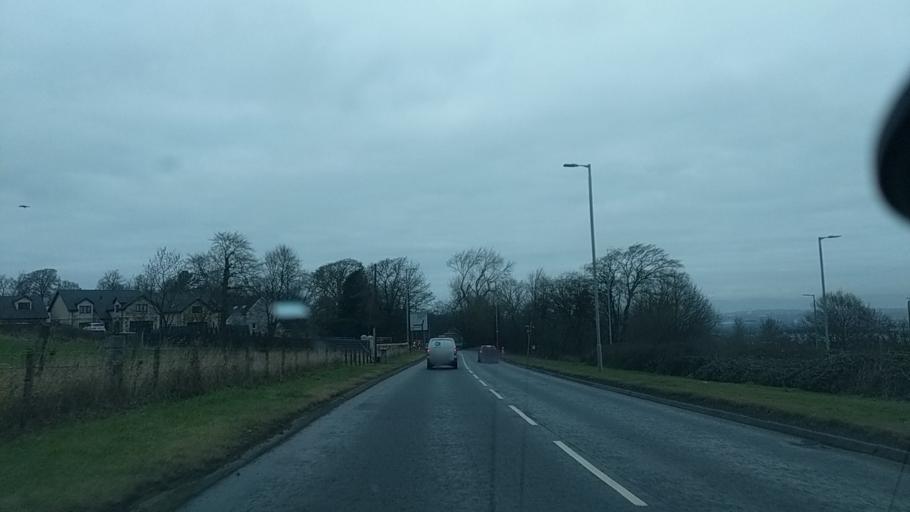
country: GB
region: Scotland
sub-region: South Lanarkshire
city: East Kilbride
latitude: 55.8025
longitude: -4.1803
